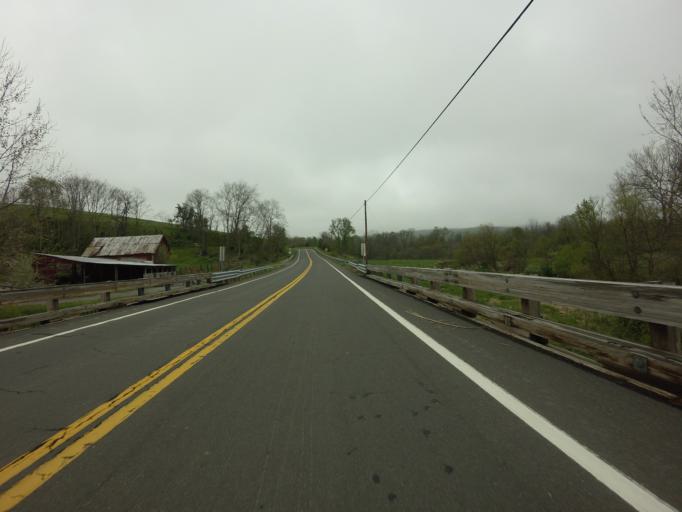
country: US
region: Maryland
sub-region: Frederick County
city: Myersville
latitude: 39.4813
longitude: -77.5375
